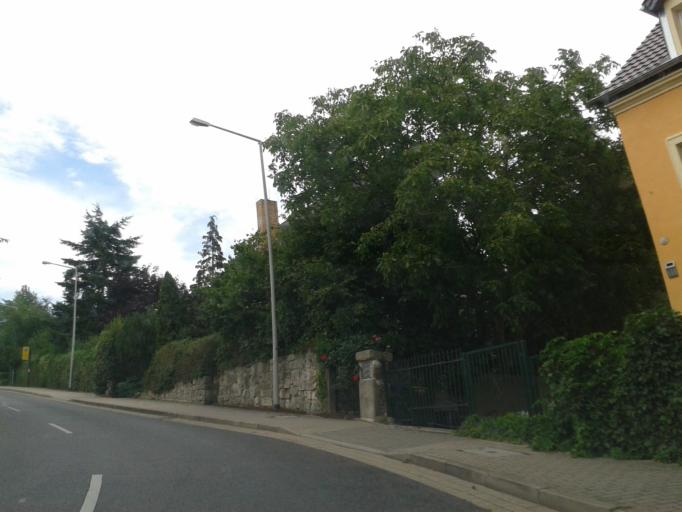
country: DE
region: Saxony
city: Bannewitz
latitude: 51.0157
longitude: 13.7291
